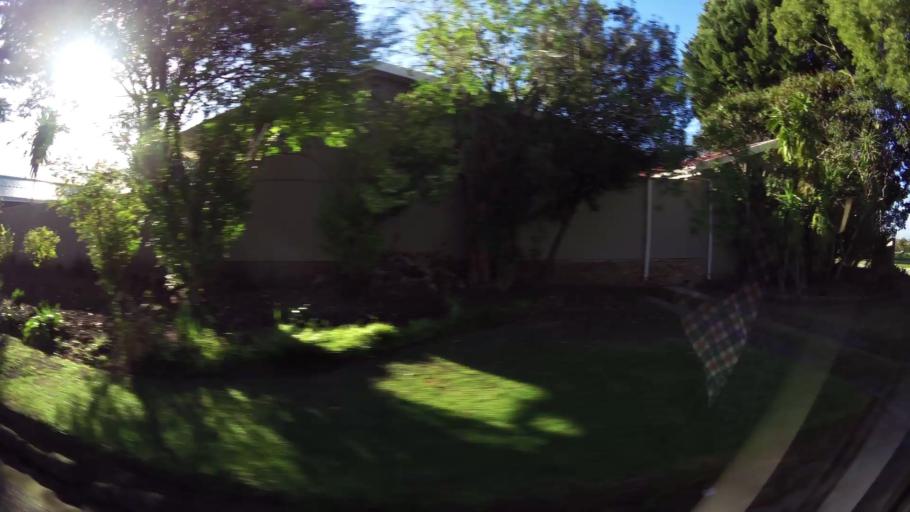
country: ZA
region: Western Cape
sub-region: Eden District Municipality
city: George
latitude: -33.9461
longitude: 22.4563
